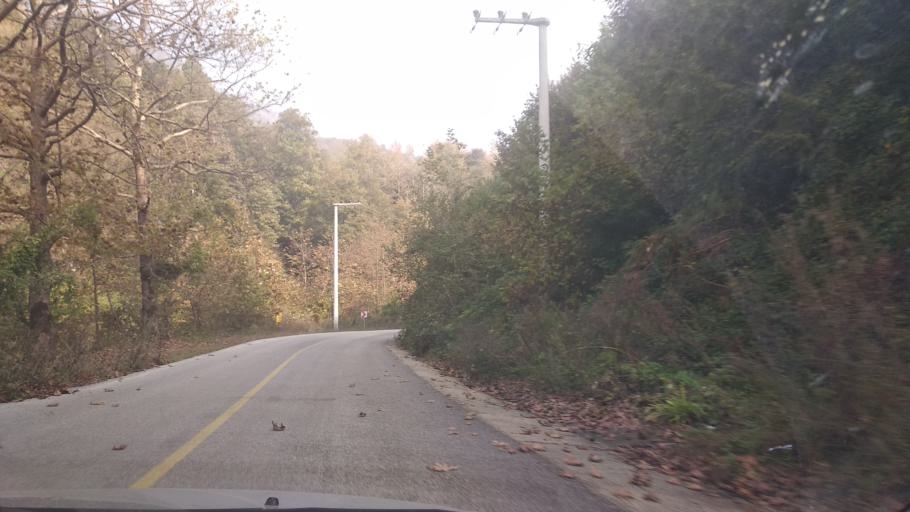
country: TR
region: Duzce
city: Kaynasli
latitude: 40.7331
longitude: 31.2224
